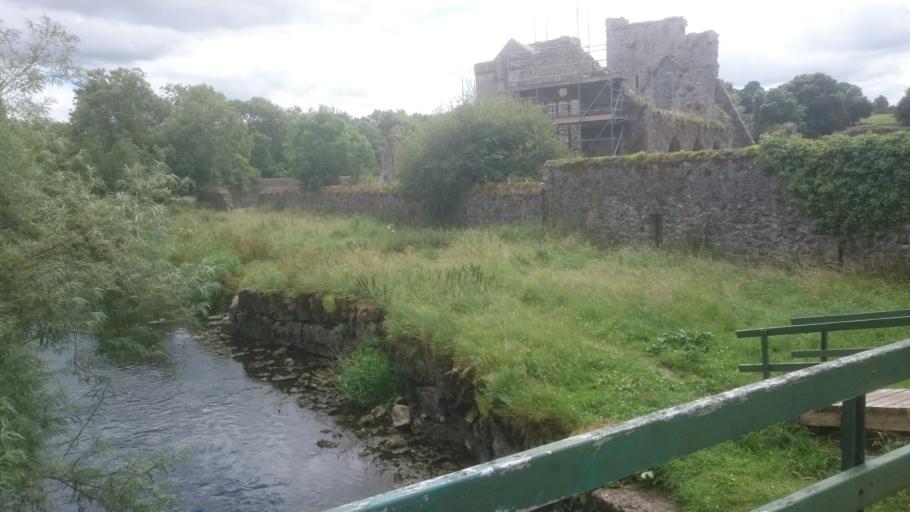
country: IE
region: Leinster
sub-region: Kilkenny
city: Kilkenny
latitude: 52.5396
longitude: -7.2667
